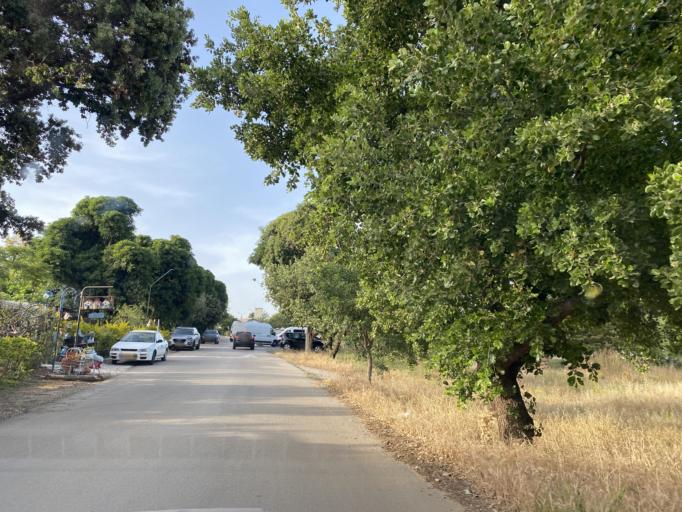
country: IL
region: Tel Aviv
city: Ramat HaSharon
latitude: 32.1551
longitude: 34.8313
